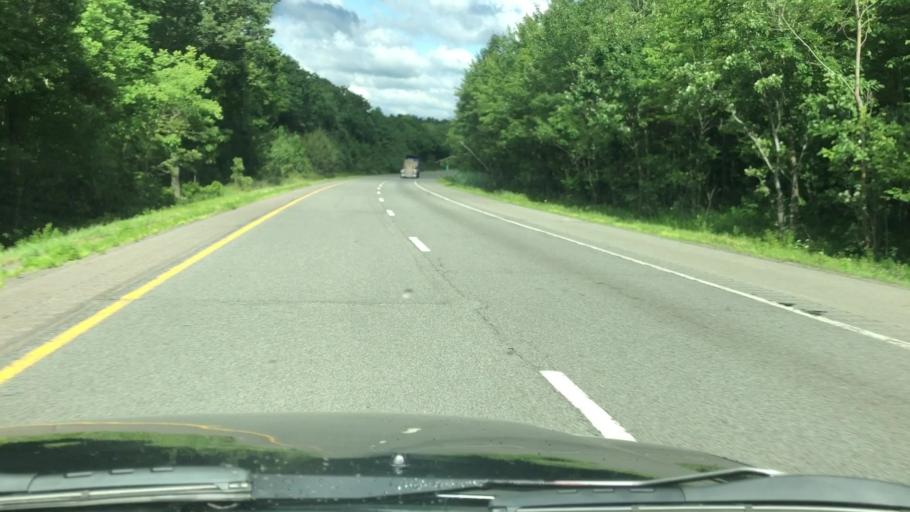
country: US
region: Pennsylvania
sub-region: Pike County
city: Hemlock Farms
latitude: 41.3674
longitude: -75.1364
